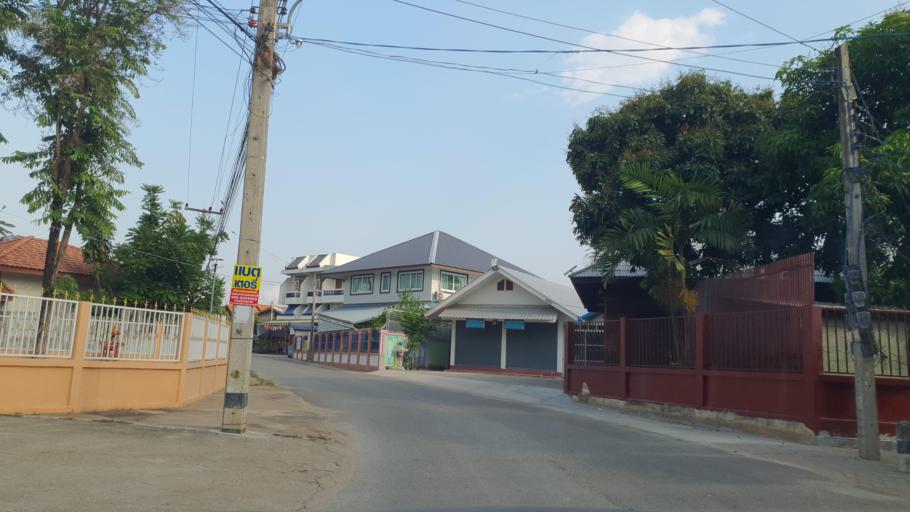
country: TH
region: Chiang Mai
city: Mae Wang
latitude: 18.6735
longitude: 98.8122
